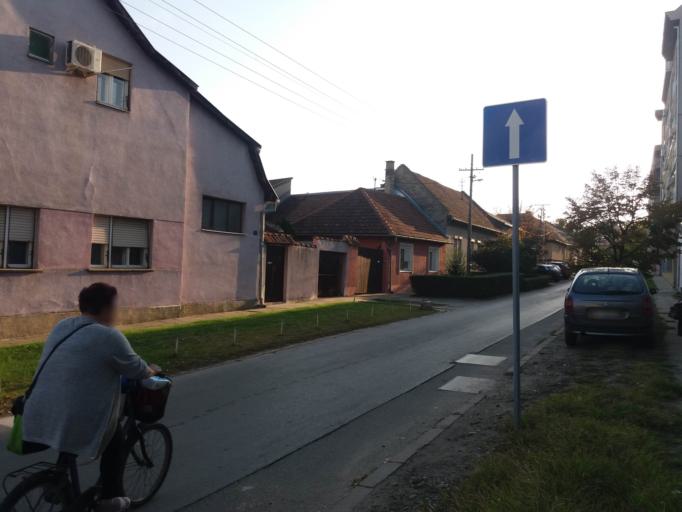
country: RS
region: Autonomna Pokrajina Vojvodina
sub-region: Severnobacki Okrug
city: Subotica
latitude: 46.0945
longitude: 19.6645
